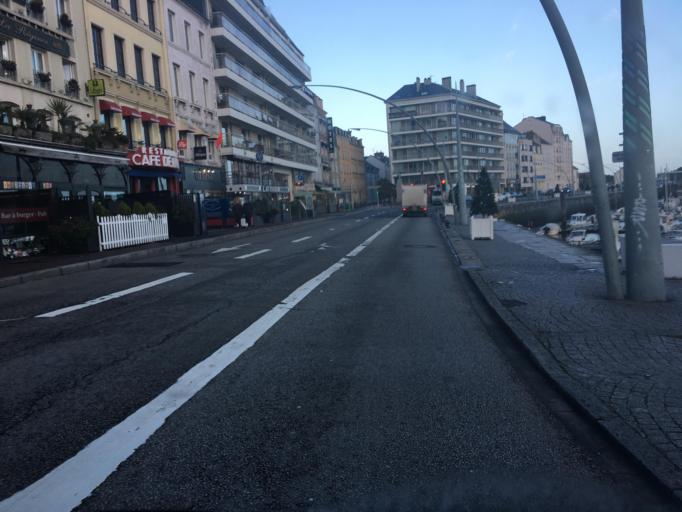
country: FR
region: Lower Normandy
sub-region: Departement de la Manche
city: Cherbourg-Octeville
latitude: 49.6394
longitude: -1.6211
